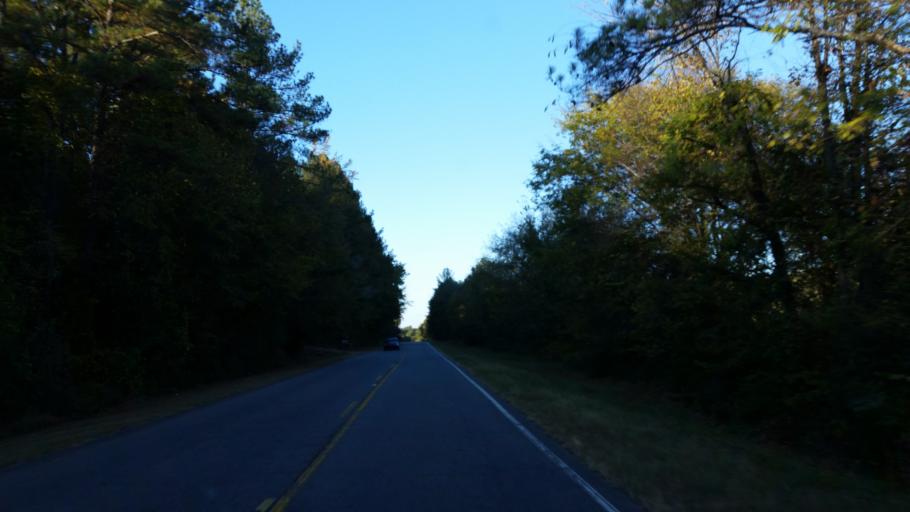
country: US
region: Georgia
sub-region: Bartow County
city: Adairsville
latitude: 34.3150
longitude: -84.9370
